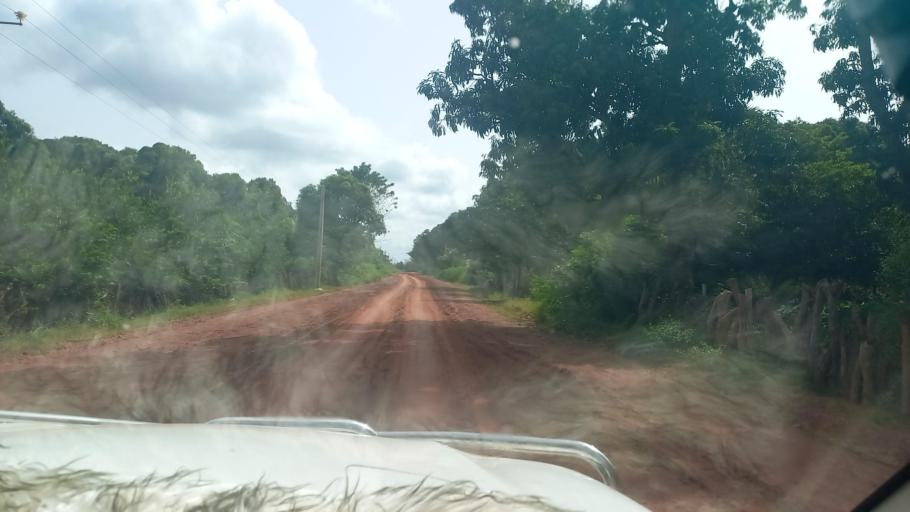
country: SN
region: Ziguinchor
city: Bignona
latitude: 12.7567
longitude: -16.2678
